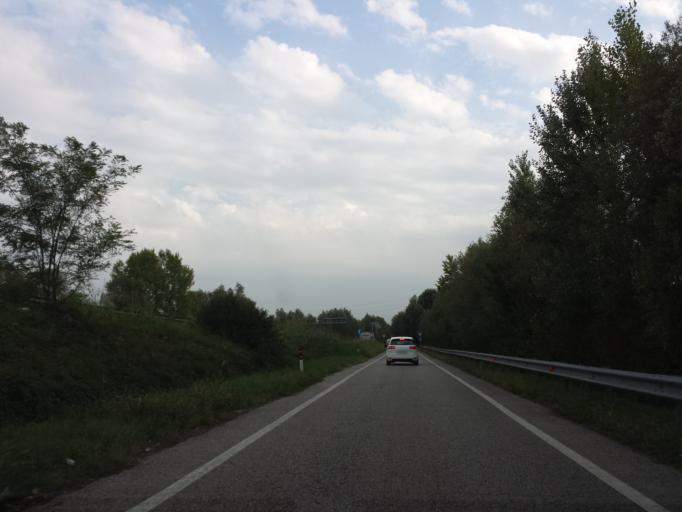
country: IT
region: Veneto
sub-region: Provincia di Padova
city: Mejaniga
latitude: 45.4639
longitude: 11.9210
